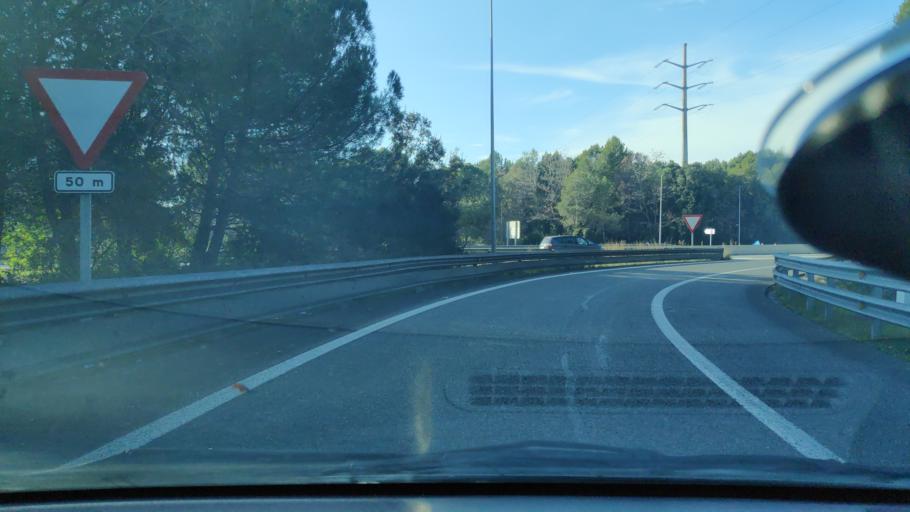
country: ES
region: Catalonia
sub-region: Provincia de Barcelona
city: Rubi
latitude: 41.4881
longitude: 2.0610
